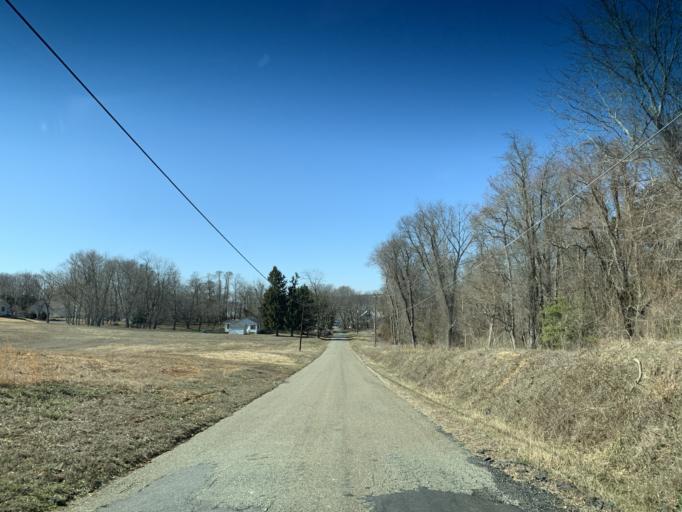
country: US
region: Maryland
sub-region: Cecil County
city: Charlestown
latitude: 39.4468
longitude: -75.9711
